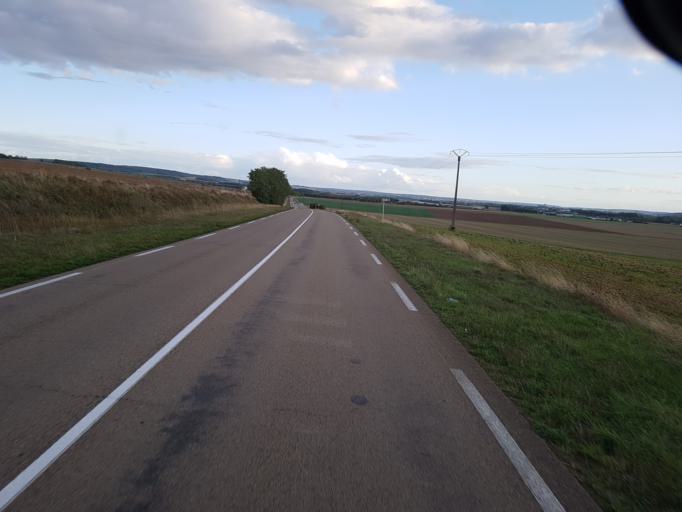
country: FR
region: Bourgogne
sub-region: Departement de l'Yonne
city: Soucy
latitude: 48.2721
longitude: 3.2738
